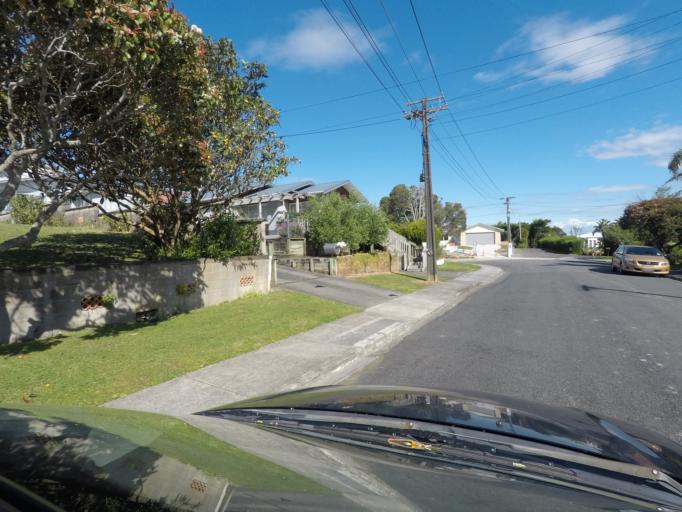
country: NZ
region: Auckland
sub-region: Auckland
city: Rosebank
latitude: -36.8596
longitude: 174.6555
